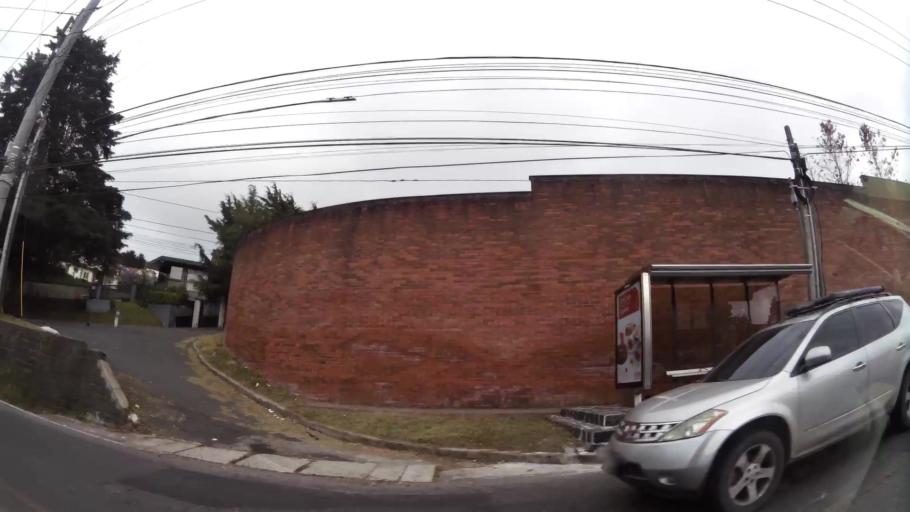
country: GT
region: Guatemala
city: Santa Catarina Pinula
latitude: 14.5630
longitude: -90.4726
